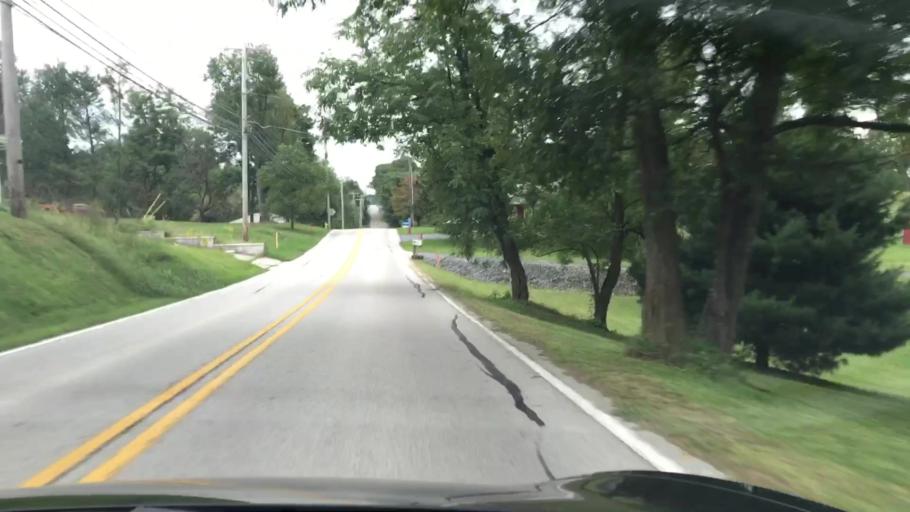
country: US
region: Pennsylvania
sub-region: Dauphin County
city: Steelton
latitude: 40.1805
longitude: -76.8546
